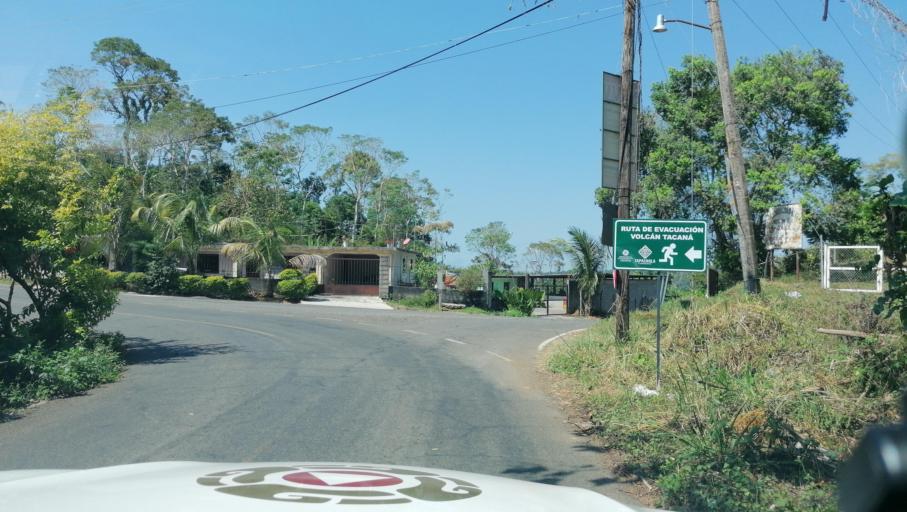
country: MX
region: Chiapas
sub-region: Cacahoatan
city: Benito Juarez
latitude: 15.0228
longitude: -92.2214
